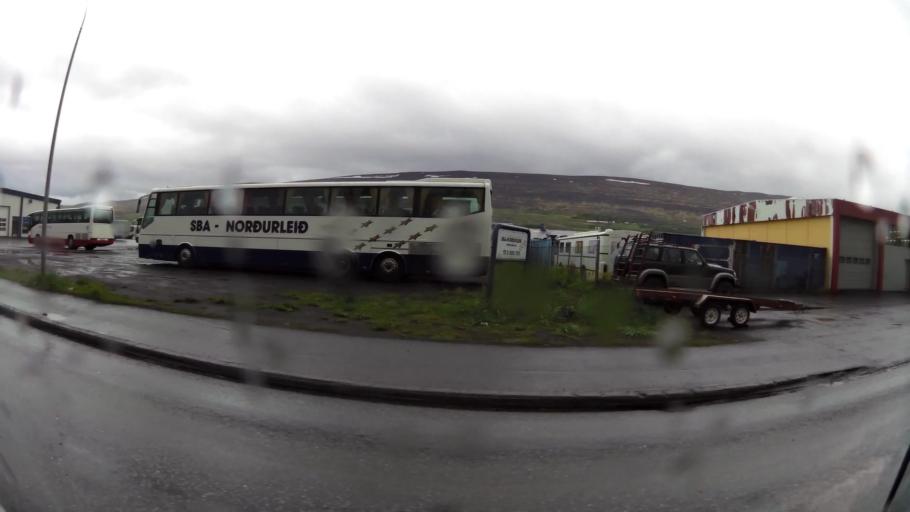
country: IS
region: Northeast
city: Akureyri
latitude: 65.6876
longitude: -18.0845
